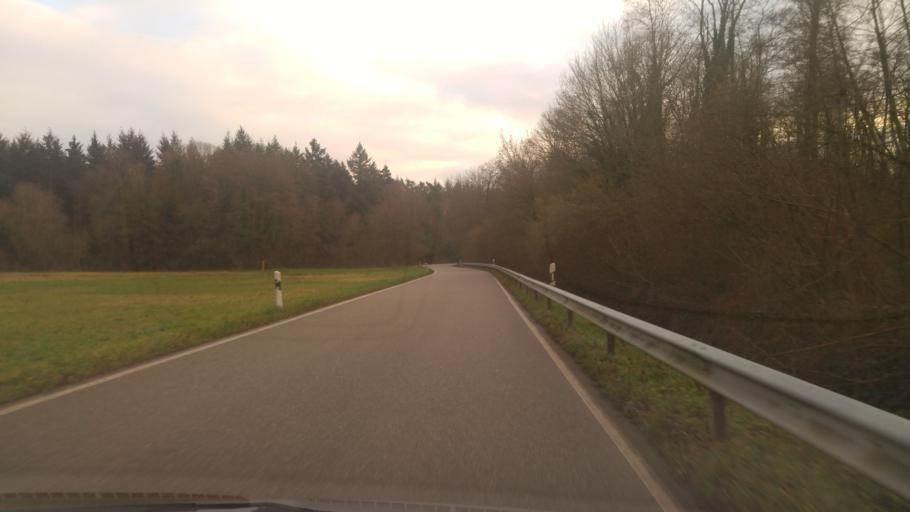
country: DE
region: Rheinland-Pfalz
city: Minfeld
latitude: 49.0571
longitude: 8.1647
